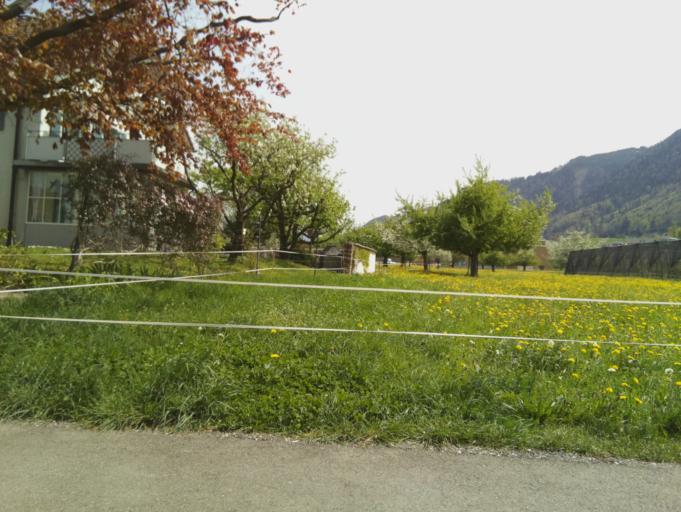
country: CH
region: Schwyz
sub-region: Bezirk March
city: Schubelbach
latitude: 47.1750
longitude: 8.8908
